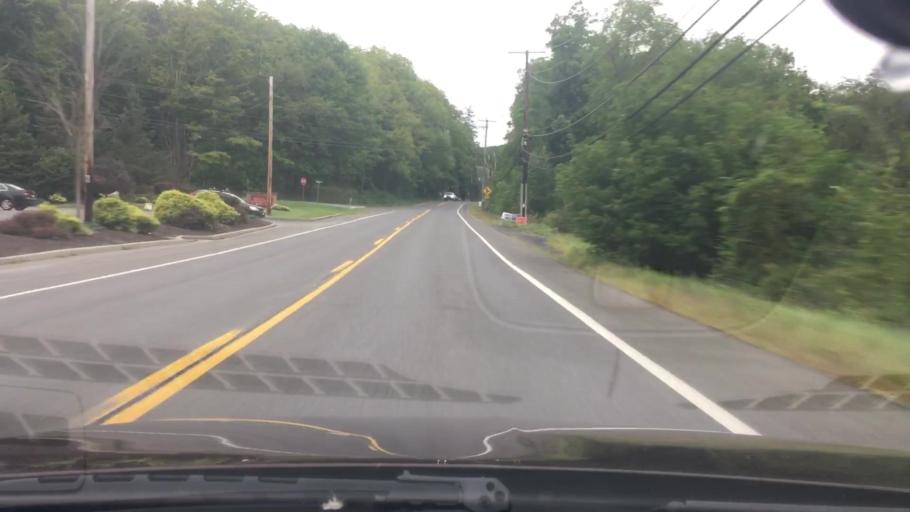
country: US
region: New York
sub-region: Dutchess County
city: Millbrook
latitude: 41.7804
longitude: -73.7486
